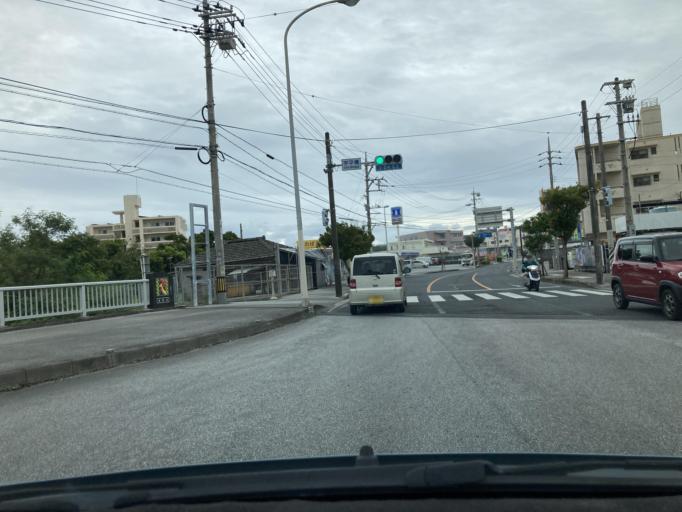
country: JP
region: Okinawa
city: Tomigusuku
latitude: 26.1789
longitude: 127.7180
